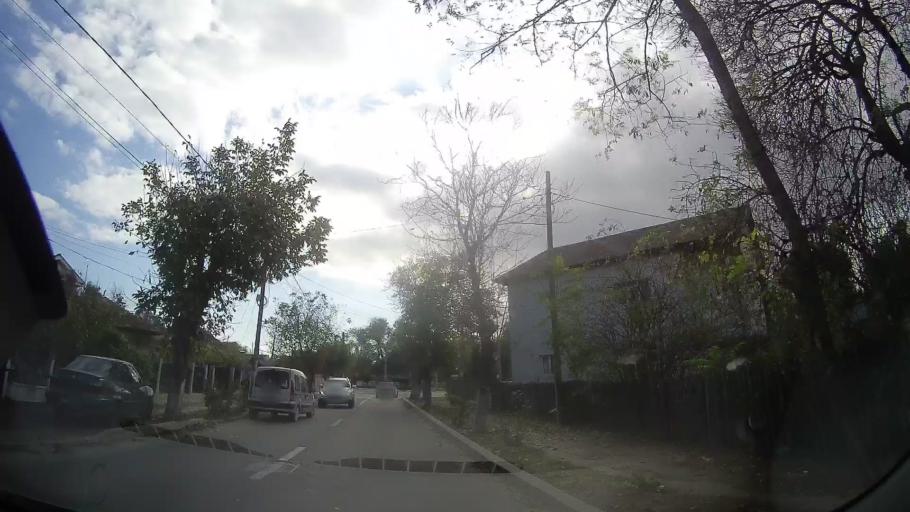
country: RO
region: Constanta
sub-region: Oras Techirghiol
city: Techirghiol
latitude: 44.0562
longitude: 28.6007
